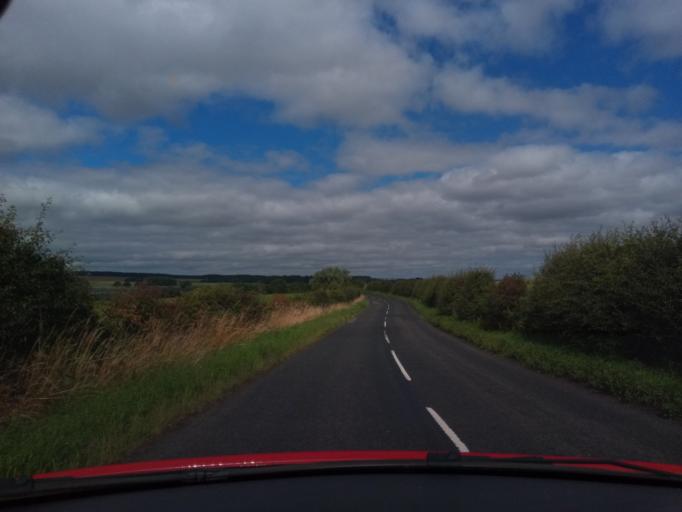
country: GB
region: Scotland
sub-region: The Scottish Borders
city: Kelso
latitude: 55.5397
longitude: -2.3697
